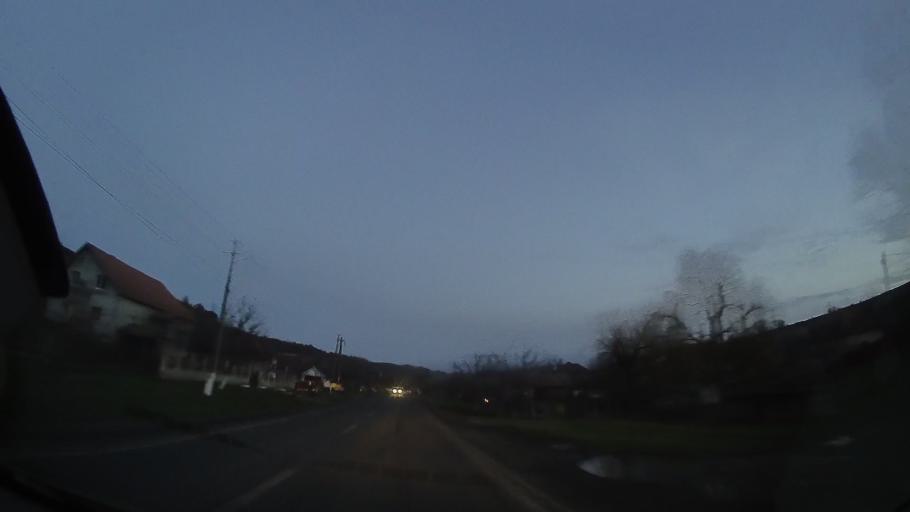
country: RO
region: Mures
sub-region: Comuna Sarmasu
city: Sarmasu
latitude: 46.7884
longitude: 24.1986
